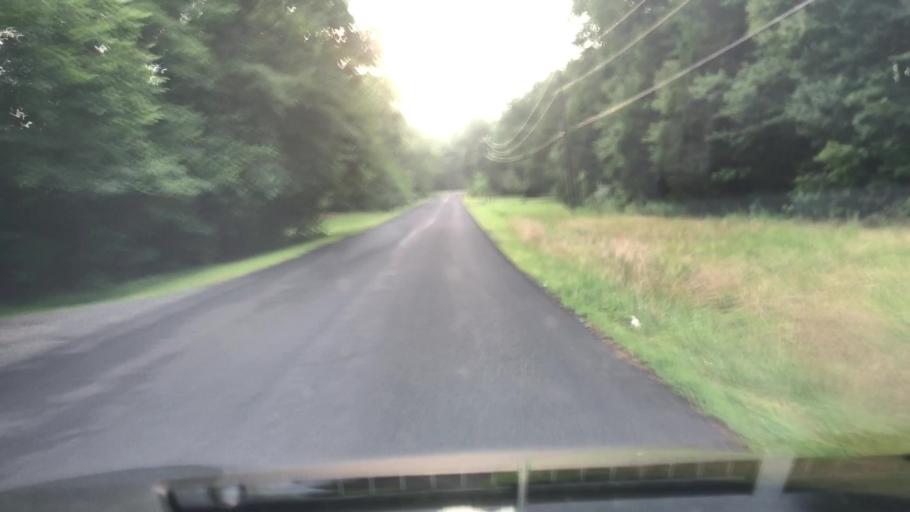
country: US
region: Virginia
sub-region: Fauquier County
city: New Baltimore
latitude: 38.7125
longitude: -77.6683
